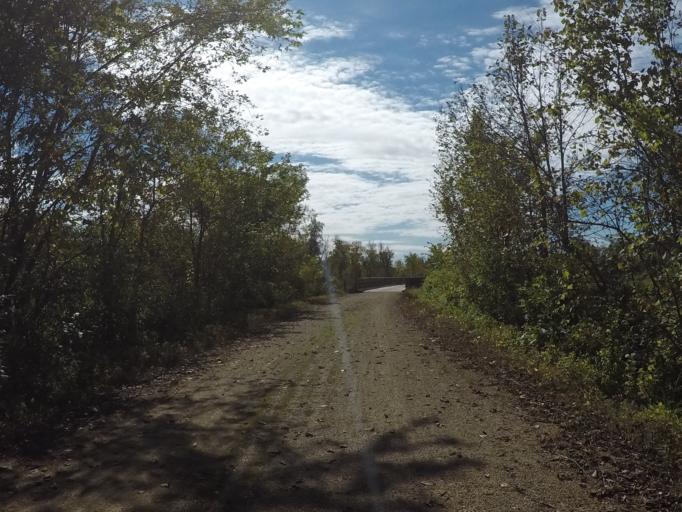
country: US
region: Wisconsin
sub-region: Richland County
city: Richland Center
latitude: 43.2631
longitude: -90.3025
